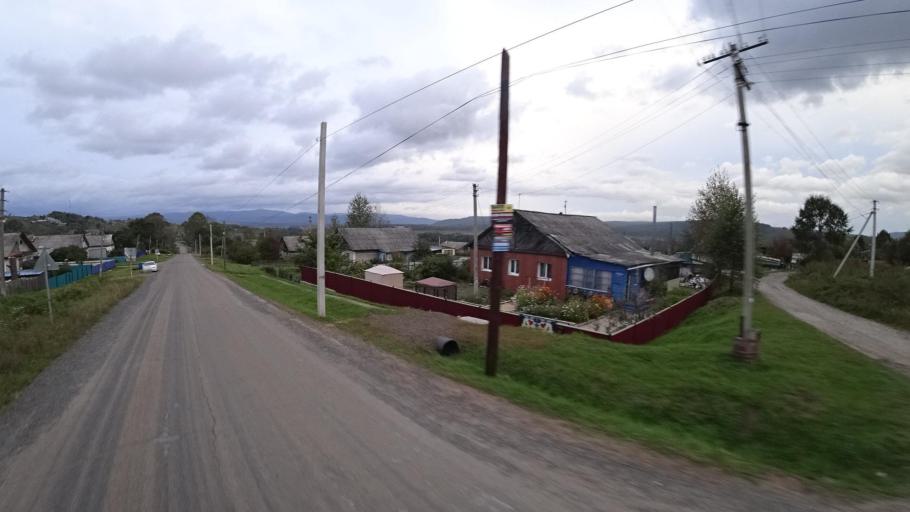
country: RU
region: Jewish Autonomous Oblast
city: Izvestkovyy
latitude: 48.9689
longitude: 131.5860
